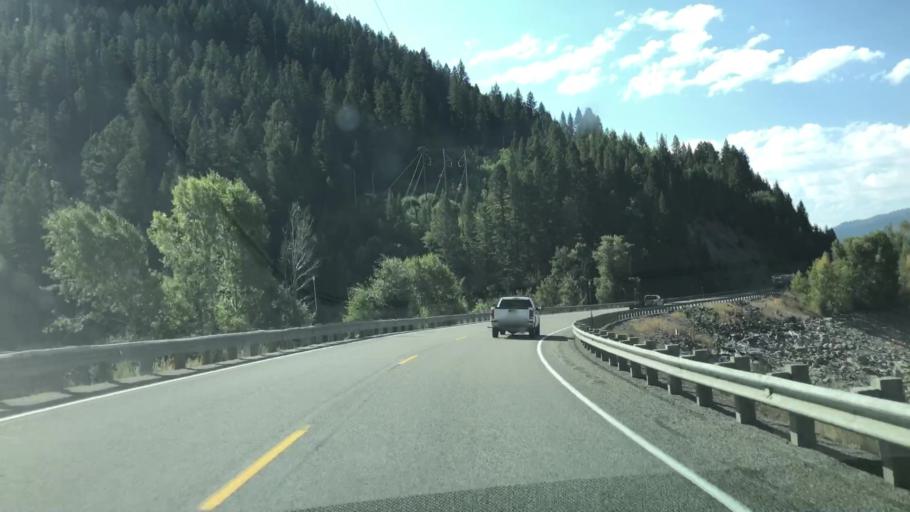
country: US
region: Idaho
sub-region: Teton County
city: Victor
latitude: 43.3184
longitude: -111.1448
